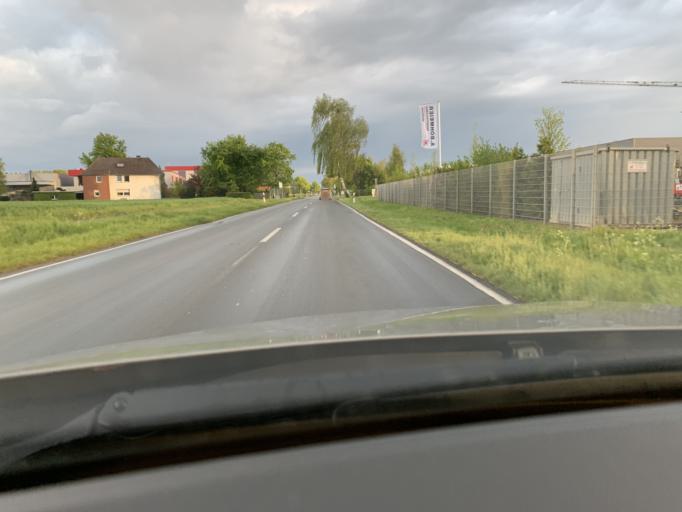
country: DE
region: North Rhine-Westphalia
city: Rietberg
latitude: 51.7695
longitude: 8.3852
